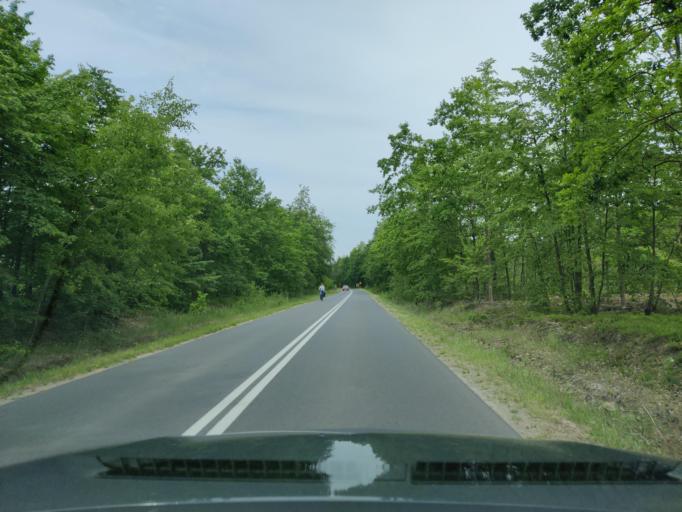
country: PL
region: Masovian Voivodeship
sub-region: Powiat wyszkowski
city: Rzasnik
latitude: 52.6795
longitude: 21.4203
